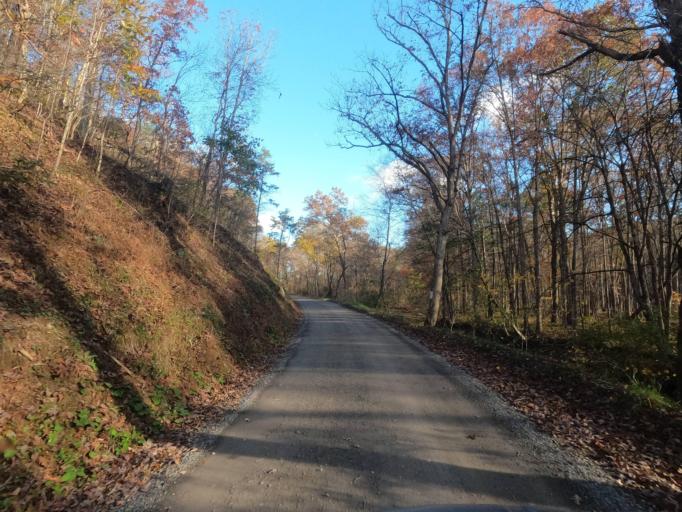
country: US
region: West Virginia
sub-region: Morgan County
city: Berkeley Springs
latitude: 39.6695
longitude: -78.4594
